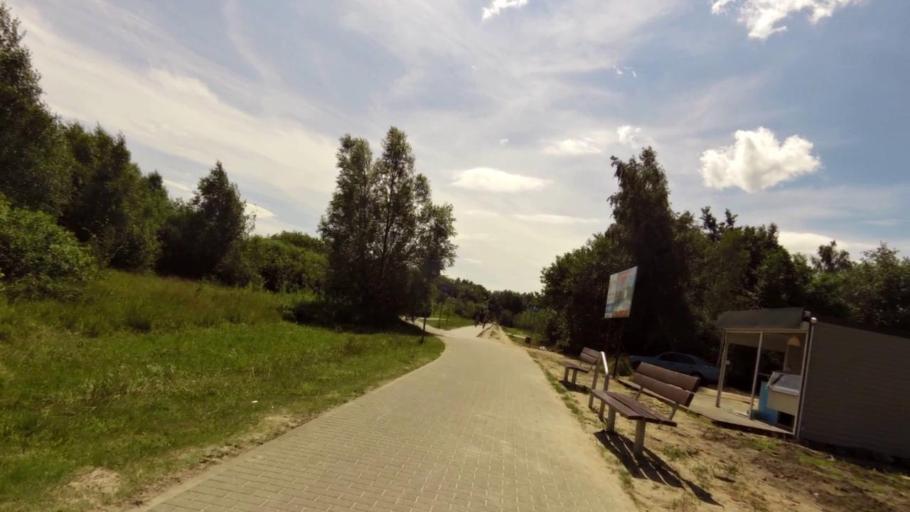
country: PL
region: West Pomeranian Voivodeship
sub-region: Powiat kolobrzeski
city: Kolobrzeg
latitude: 54.1976
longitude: 15.6605
